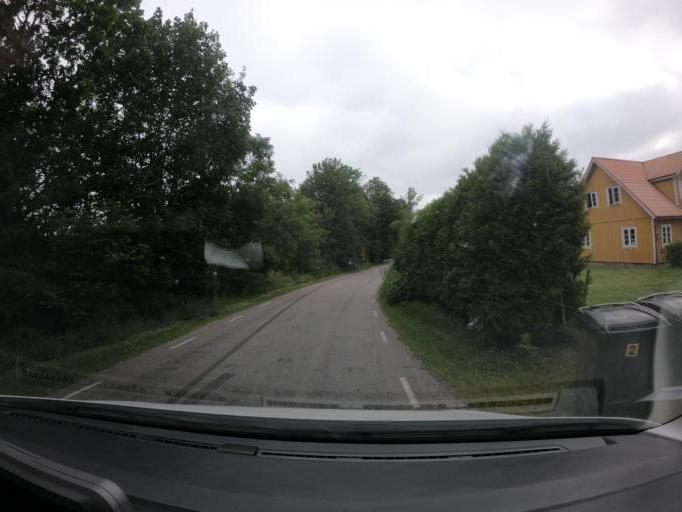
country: SE
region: Skane
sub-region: Klippans Kommun
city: Ljungbyhed
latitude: 56.0402
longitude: 13.2625
